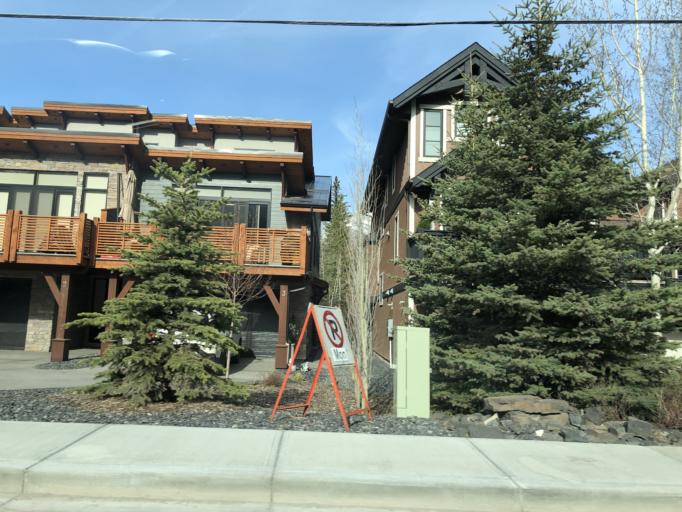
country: CA
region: Alberta
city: Canmore
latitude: 51.0833
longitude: -115.3669
